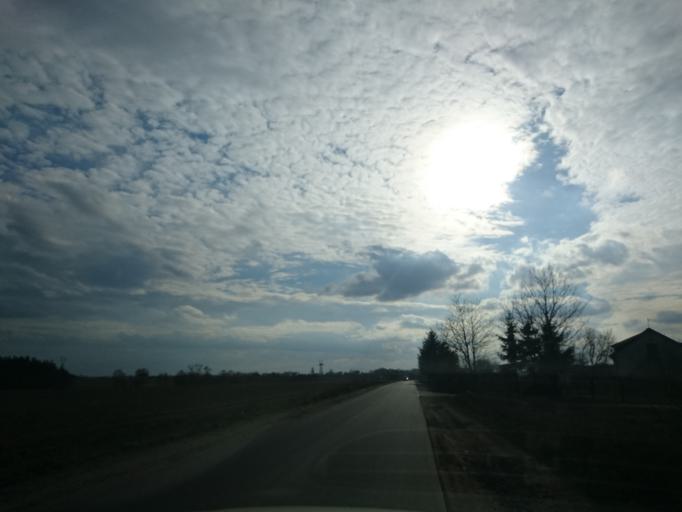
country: PL
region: Kujawsko-Pomorskie
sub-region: Powiat torunski
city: Lubicz Gorny
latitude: 53.0470
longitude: 18.8249
